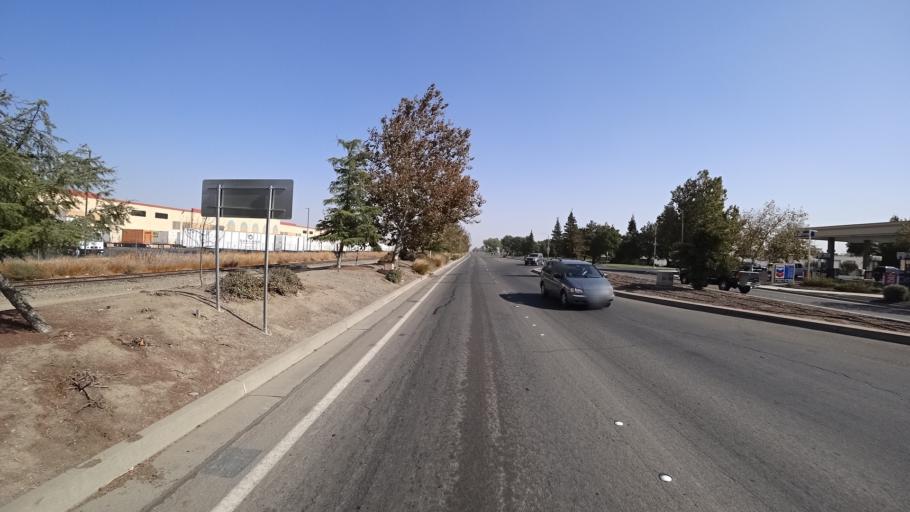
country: US
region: California
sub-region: Yolo County
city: Woodland
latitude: 38.6772
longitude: -121.7275
